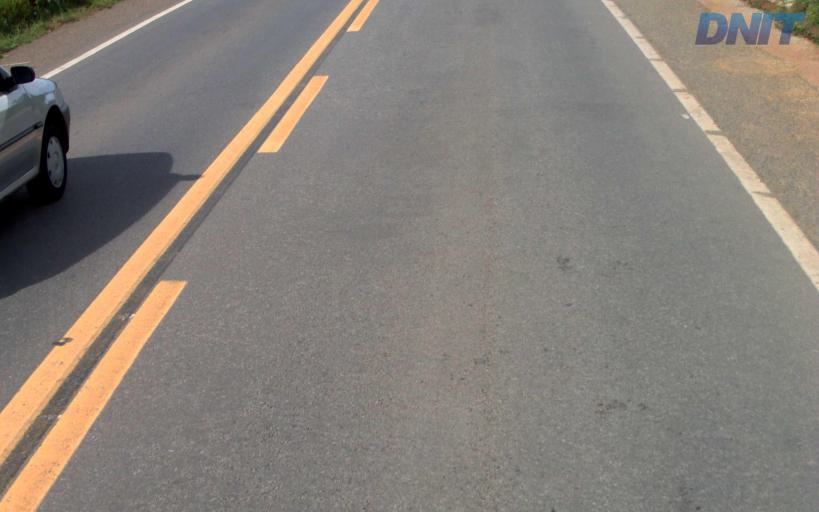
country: BR
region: Minas Gerais
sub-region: Belo Oriente
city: Belo Oriente
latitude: -19.1965
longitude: -42.2825
